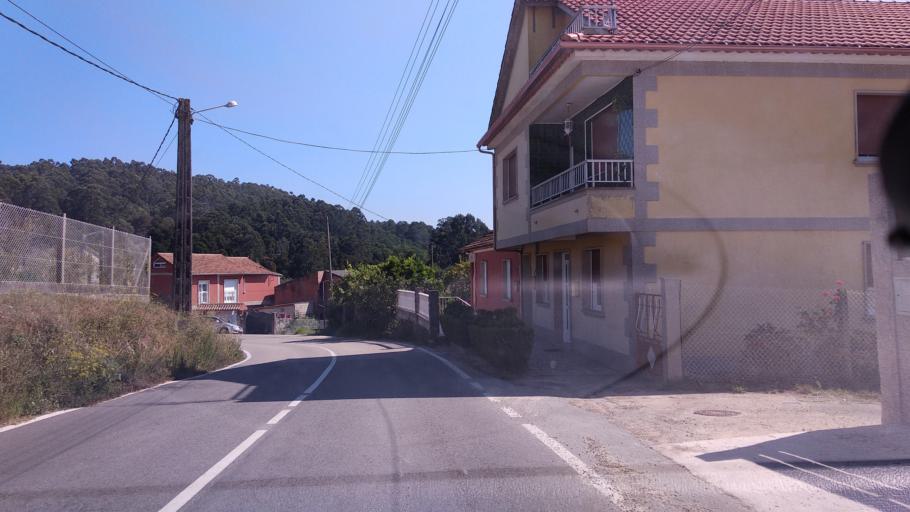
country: ES
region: Galicia
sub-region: Provincia de Pontevedra
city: Moana
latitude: 42.2762
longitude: -8.7620
